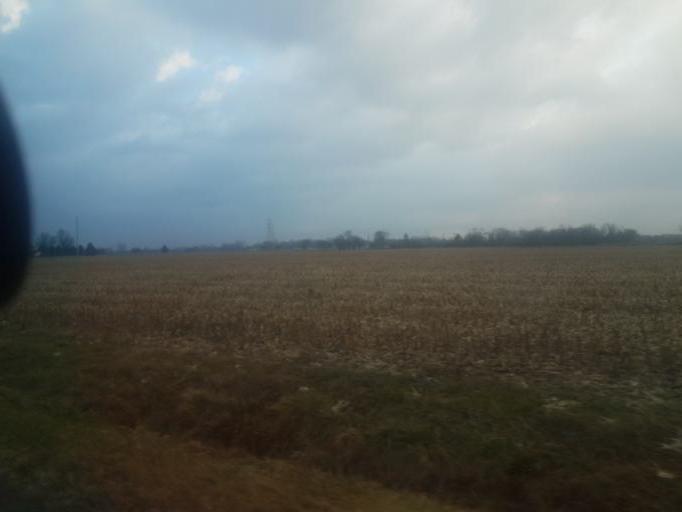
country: US
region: Ohio
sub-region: Marion County
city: Marion
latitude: 40.5985
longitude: -83.1689
